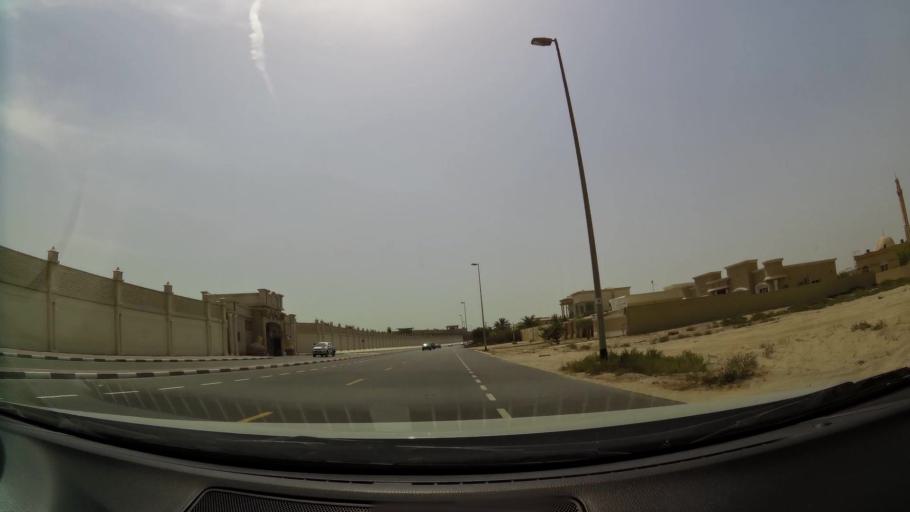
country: AE
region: Ash Shariqah
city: Sharjah
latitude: 25.2380
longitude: 55.4330
